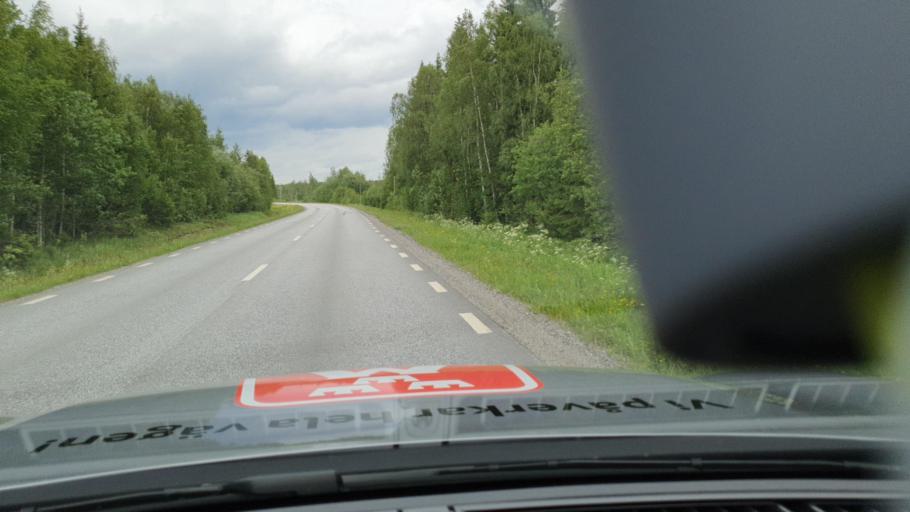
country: SE
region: Norrbotten
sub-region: Lulea Kommun
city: Lulea
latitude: 65.6682
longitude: 22.2253
